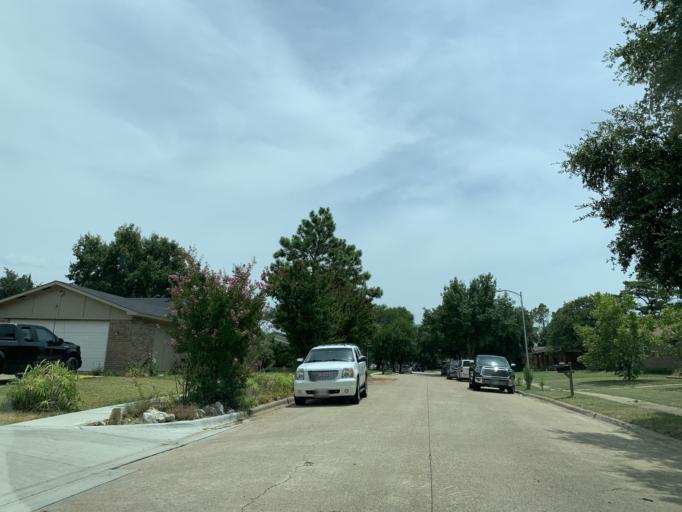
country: US
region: Texas
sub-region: Dallas County
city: Grand Prairie
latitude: 32.6588
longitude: -97.0345
